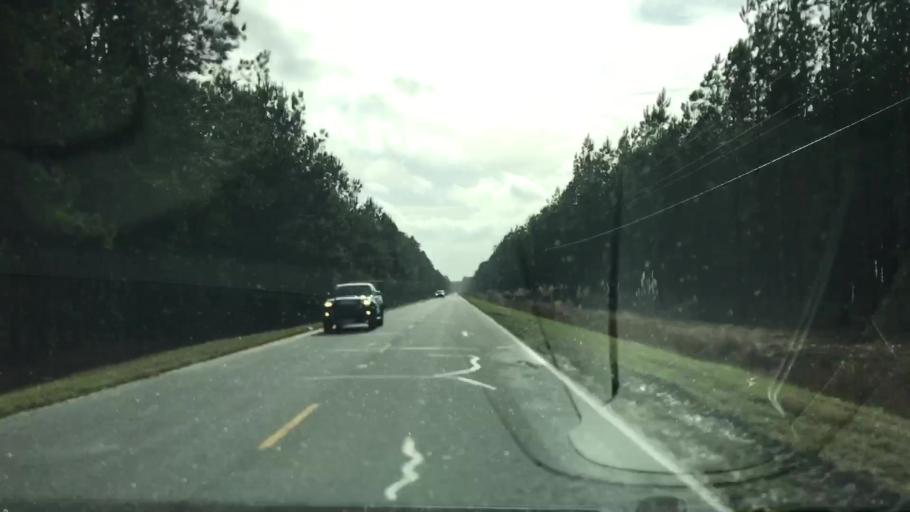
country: US
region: South Carolina
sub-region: Williamsburg County
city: Andrews
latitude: 33.4033
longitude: -79.6135
